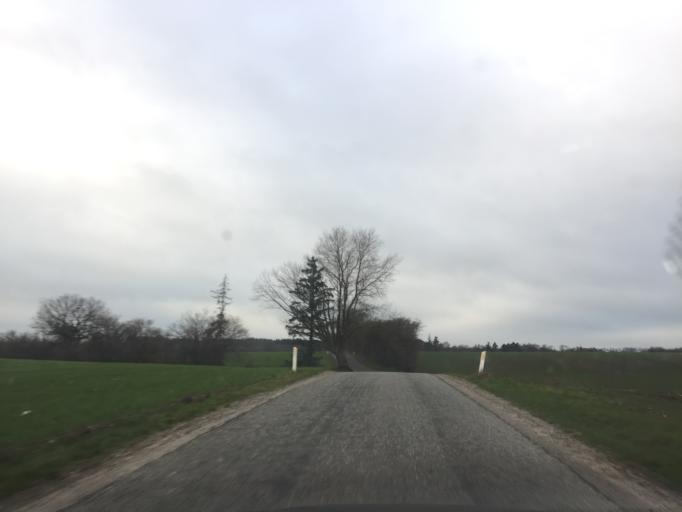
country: DK
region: South Denmark
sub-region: Nyborg Kommune
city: Nyborg
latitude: 55.1920
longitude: 10.7097
